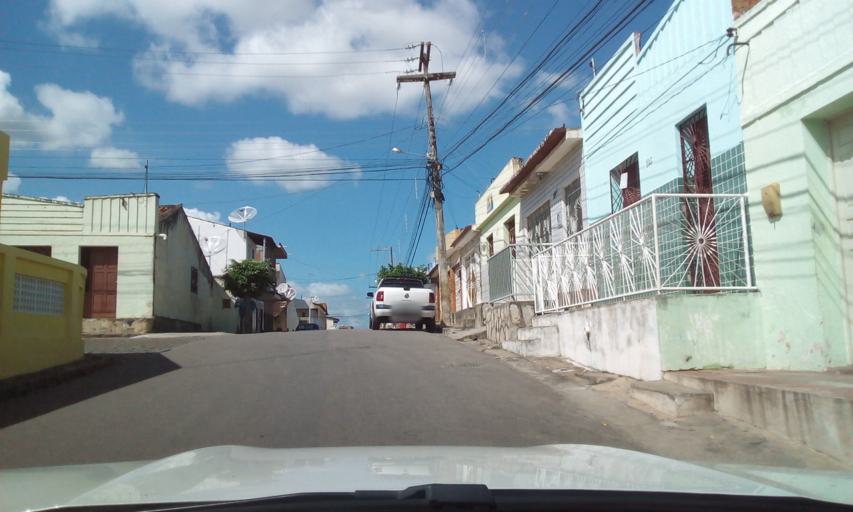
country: BR
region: Paraiba
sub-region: Guarabira
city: Guarabira
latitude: -6.8554
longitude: -35.4820
